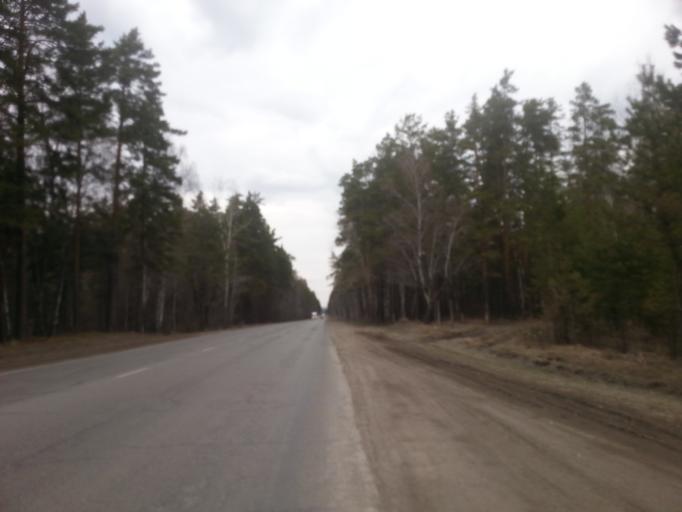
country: RU
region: Altai Krai
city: Yuzhnyy
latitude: 53.2747
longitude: 83.7215
